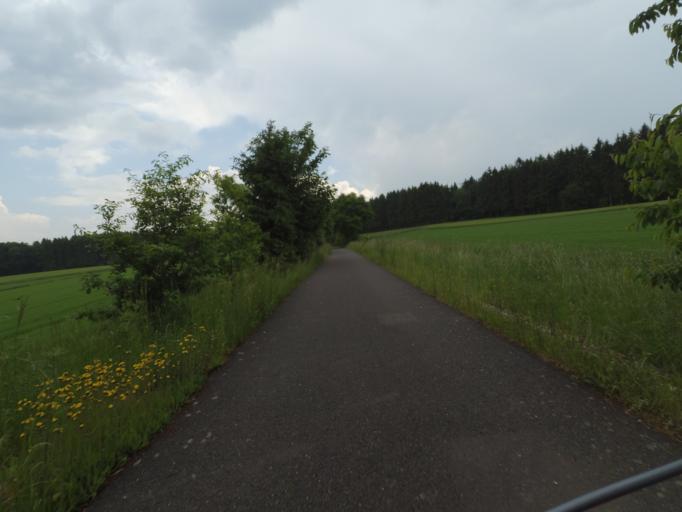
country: DE
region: Rheinland-Pfalz
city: Hollnich
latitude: 50.0698
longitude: 7.4662
